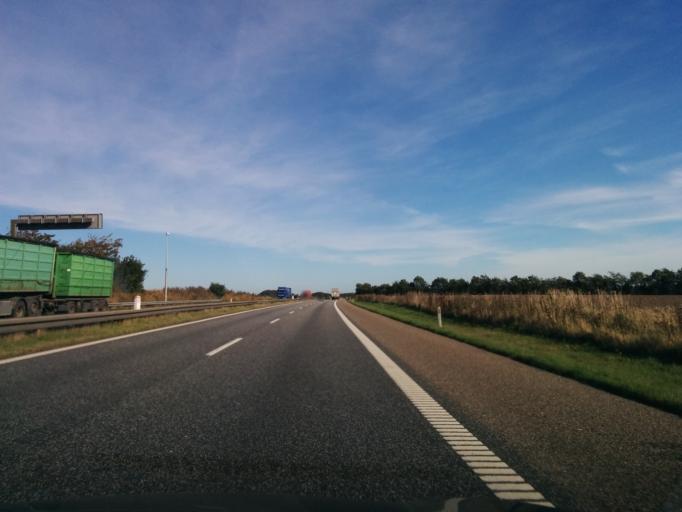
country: DK
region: South Denmark
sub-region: Vejle Kommune
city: Vejle
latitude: 55.7623
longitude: 9.6099
